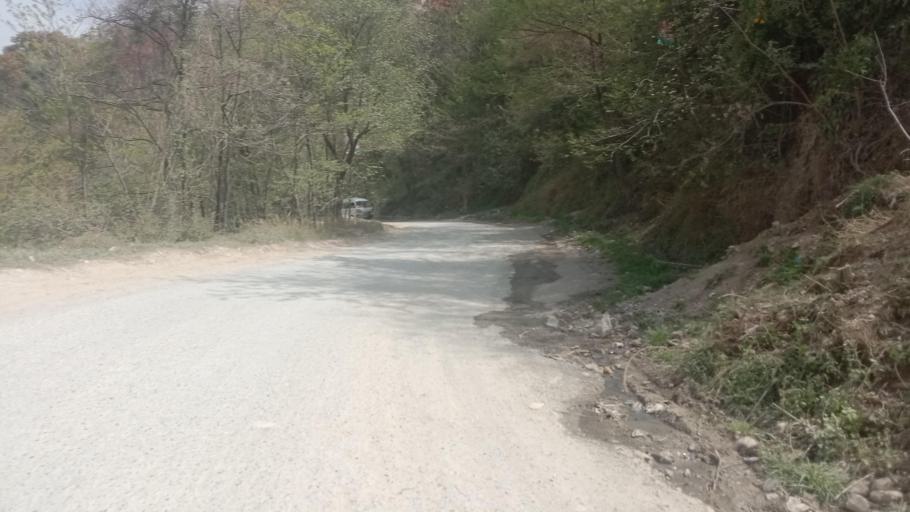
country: PK
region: Khyber Pakhtunkhwa
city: Abbottabad
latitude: 34.1584
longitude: 73.2679
